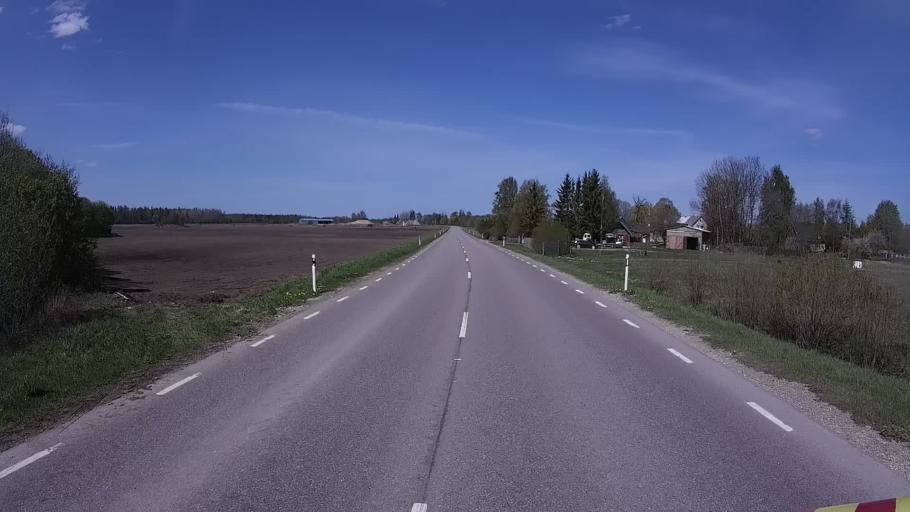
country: EE
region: Harju
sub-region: Keila linn
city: Keila
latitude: 59.3049
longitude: 24.3246
